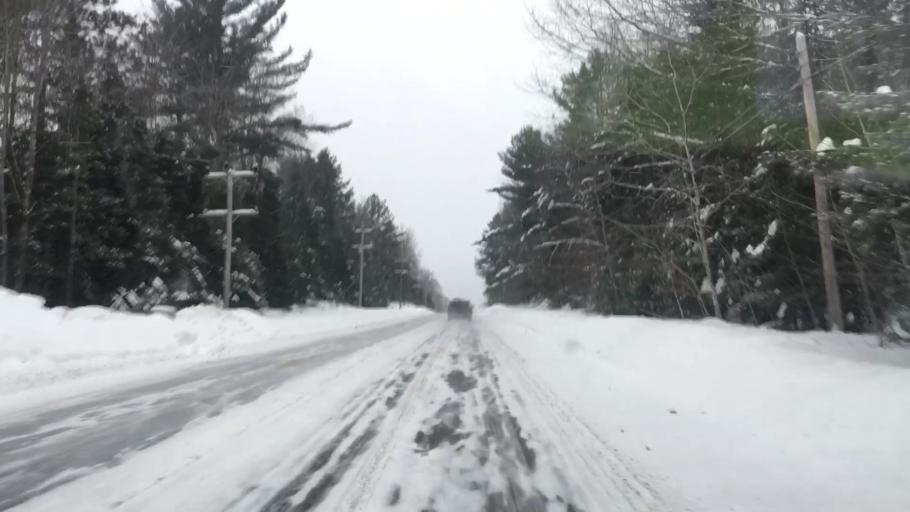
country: US
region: Maine
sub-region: Penobscot County
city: Medway
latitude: 45.5981
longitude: -68.4729
